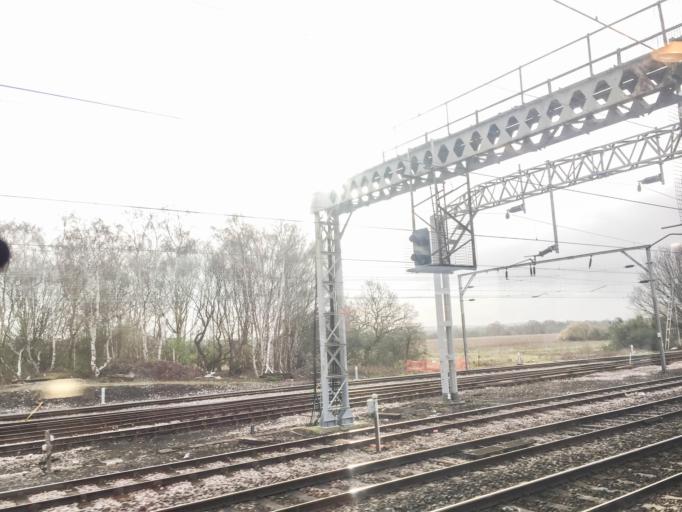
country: GB
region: England
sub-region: Cheshire East
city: Crewe
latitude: 53.0773
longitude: -2.4259
